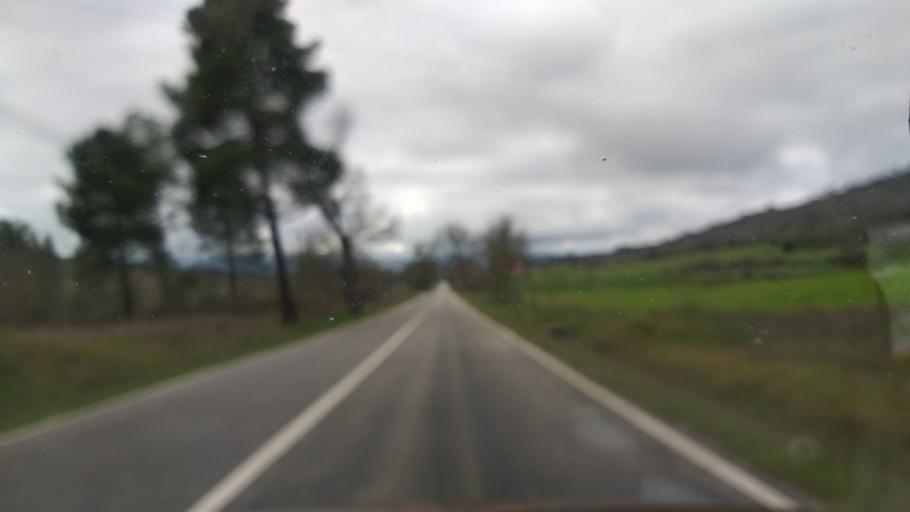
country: PT
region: Guarda
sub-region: Celorico da Beira
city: Celorico da Beira
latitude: 40.7026
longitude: -7.3665
